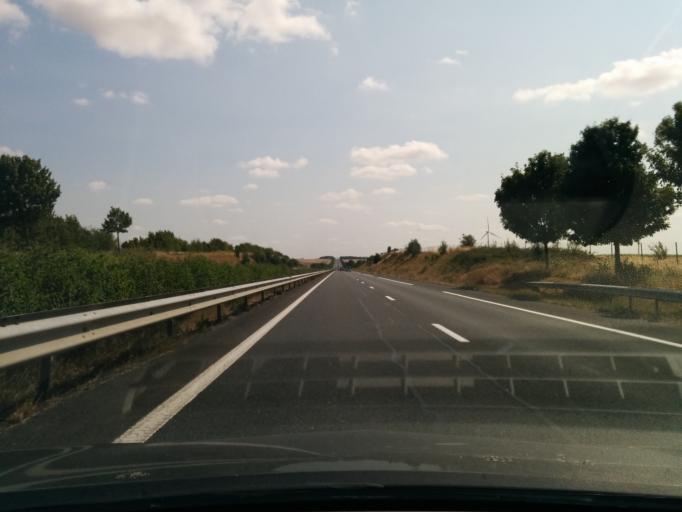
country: FR
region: Centre
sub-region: Departement de l'Indre
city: Vatan
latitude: 47.0235
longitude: 1.7873
